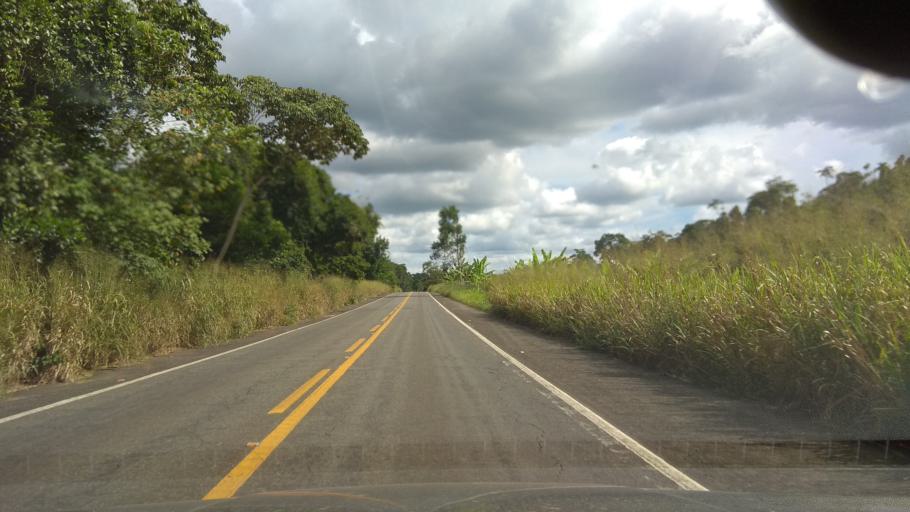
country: BR
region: Bahia
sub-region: Ubaitaba
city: Ubaitaba
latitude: -14.2482
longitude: -39.3640
